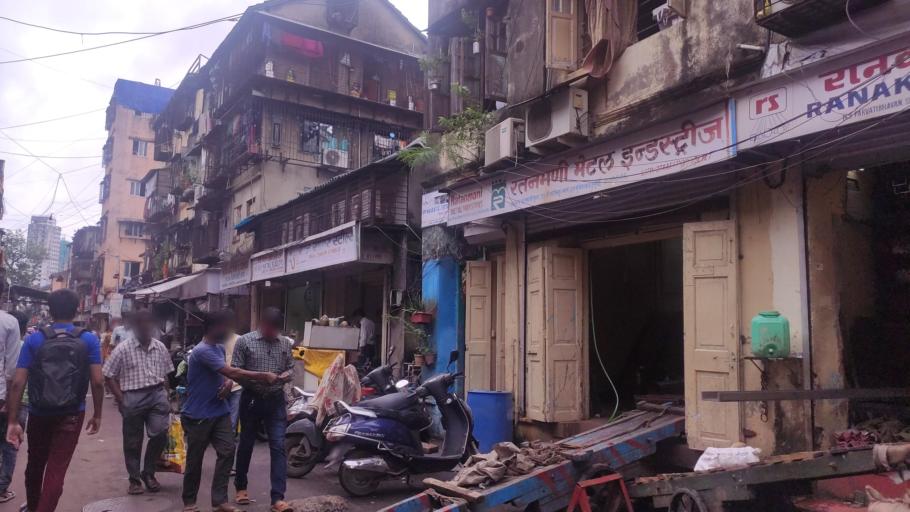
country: IN
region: Maharashtra
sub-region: Mumbai Suburban
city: Mumbai
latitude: 18.9585
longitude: 72.8273
